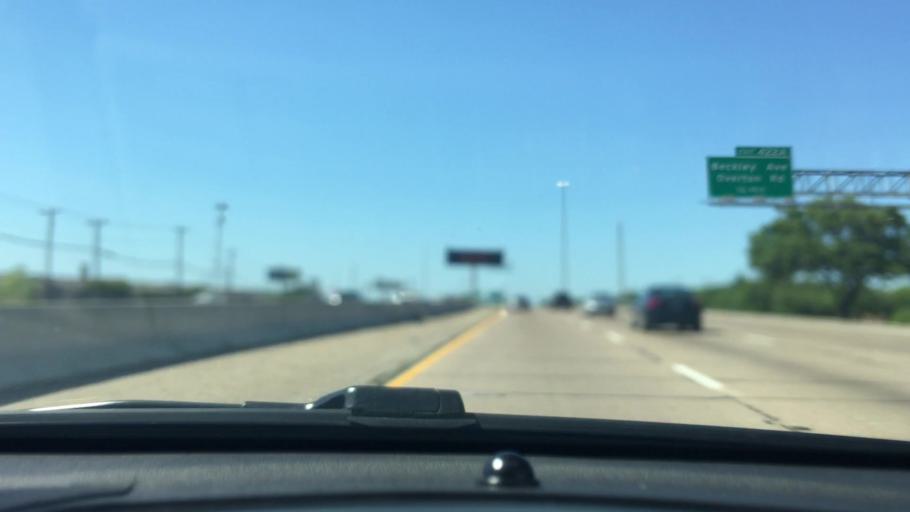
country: US
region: Texas
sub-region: Dallas County
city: Cockrell Hill
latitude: 32.6953
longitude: -96.8231
